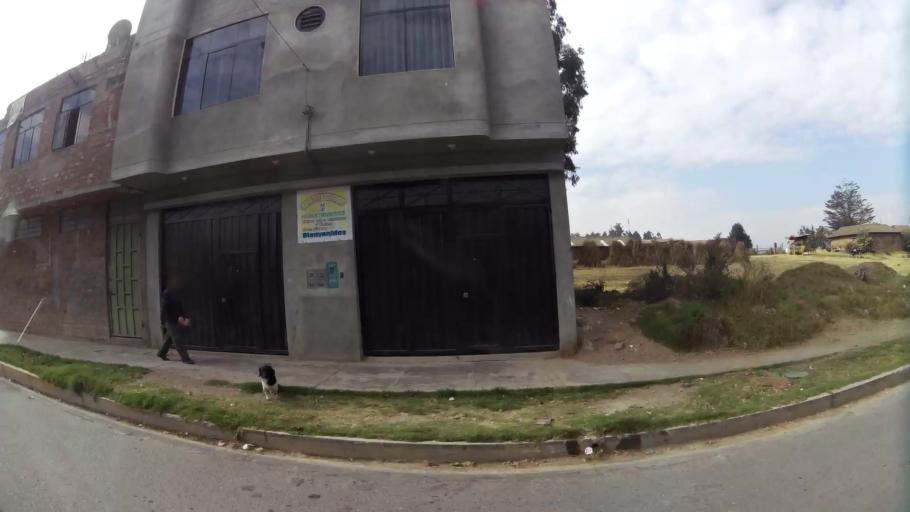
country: PE
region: Junin
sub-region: Provincia de Huancayo
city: Huancayo
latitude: -12.0555
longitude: -75.1992
